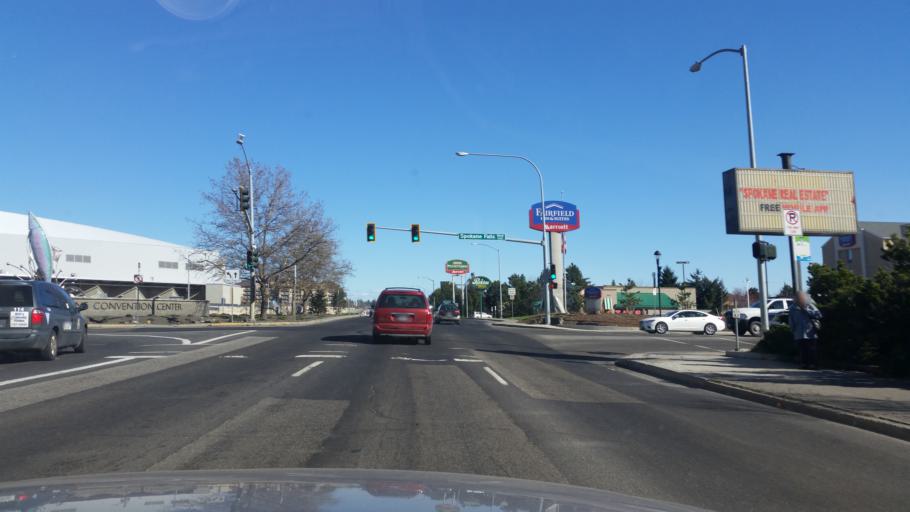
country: US
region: Washington
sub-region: Spokane County
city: Spokane
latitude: 47.6596
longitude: -117.4111
